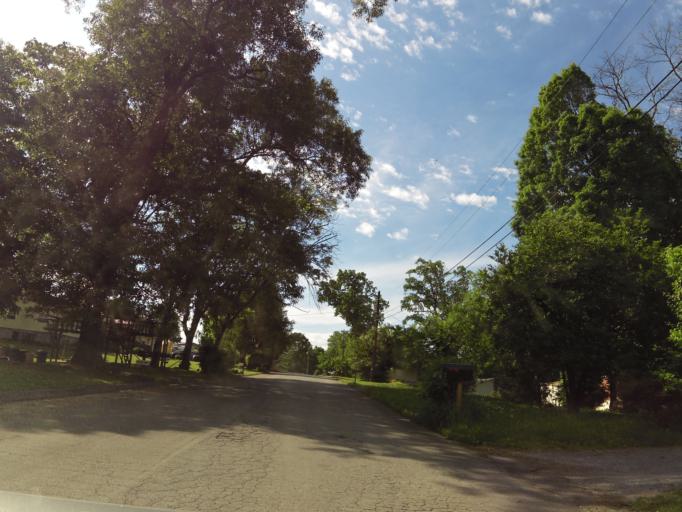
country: US
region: Tennessee
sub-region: Blount County
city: Alcoa
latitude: 35.8224
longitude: -83.9594
